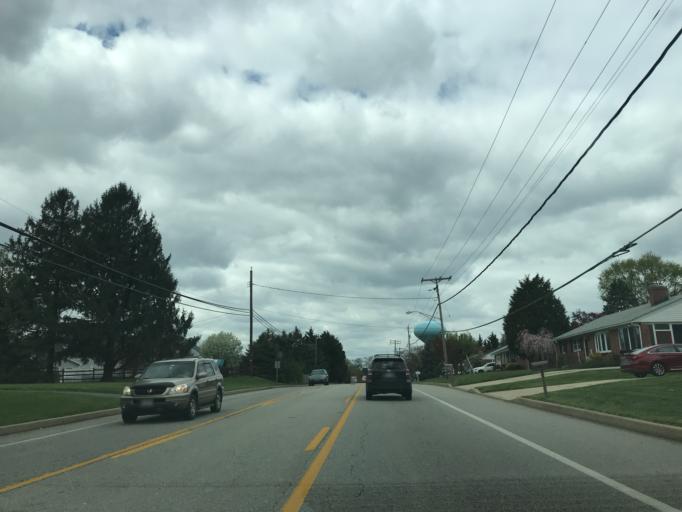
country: US
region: Maryland
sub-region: Harford County
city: Bel Air South
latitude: 39.5362
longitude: -76.3005
